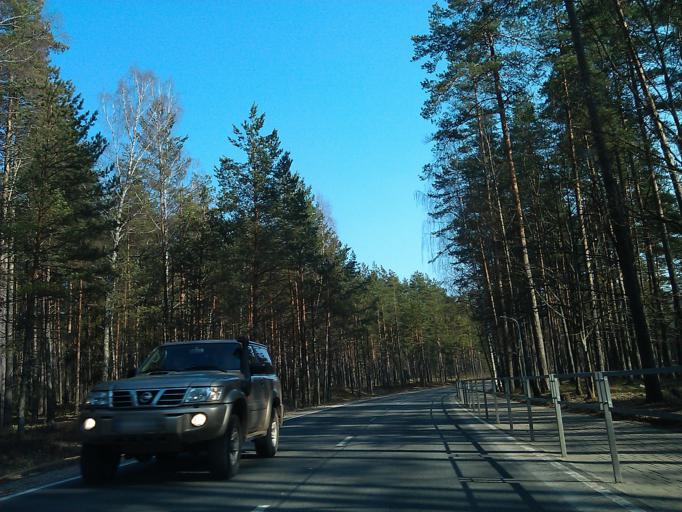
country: LV
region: Riga
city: Bergi
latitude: 56.9855
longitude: 24.3266
